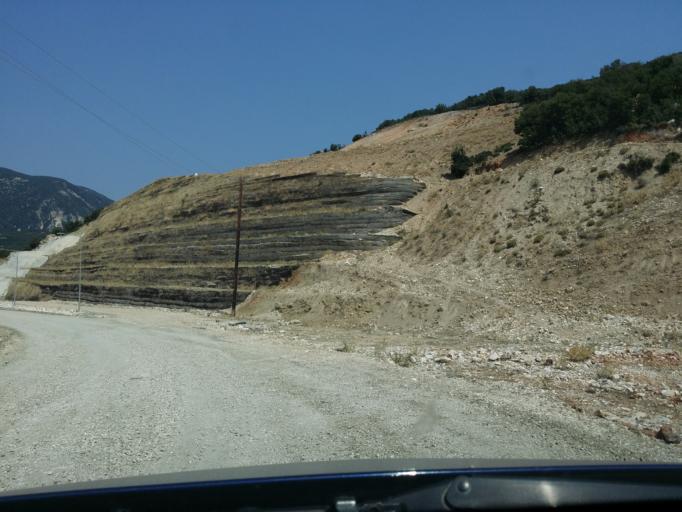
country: GR
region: West Greece
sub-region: Nomos Aitolias kai Akarnanias
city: Katouna
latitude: 38.7826
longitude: 21.0438
